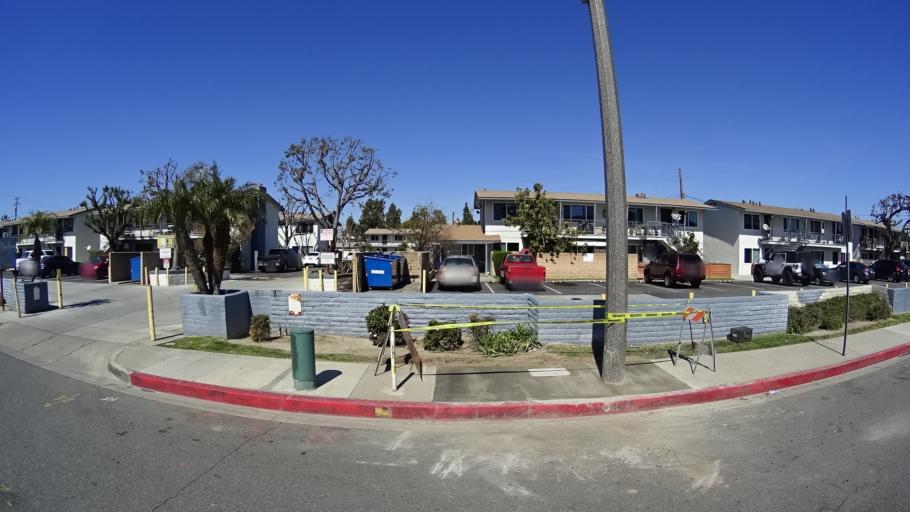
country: US
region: California
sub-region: Orange County
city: Anaheim
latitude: 33.8213
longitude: -117.9181
